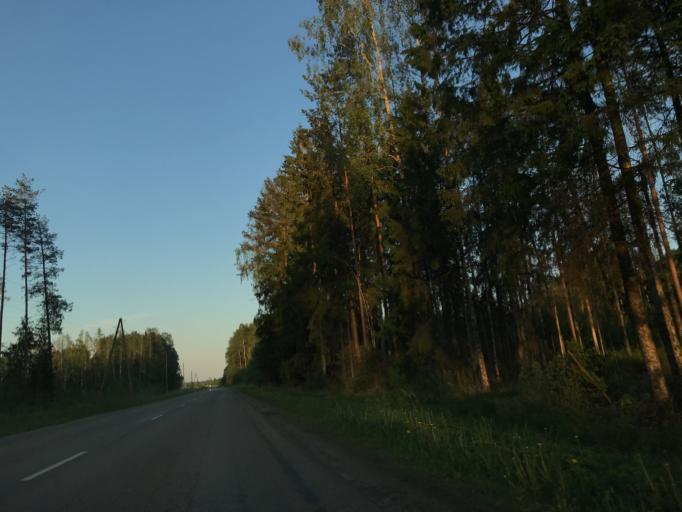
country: LV
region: Ogre
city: Jumprava
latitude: 56.4561
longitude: 24.8513
